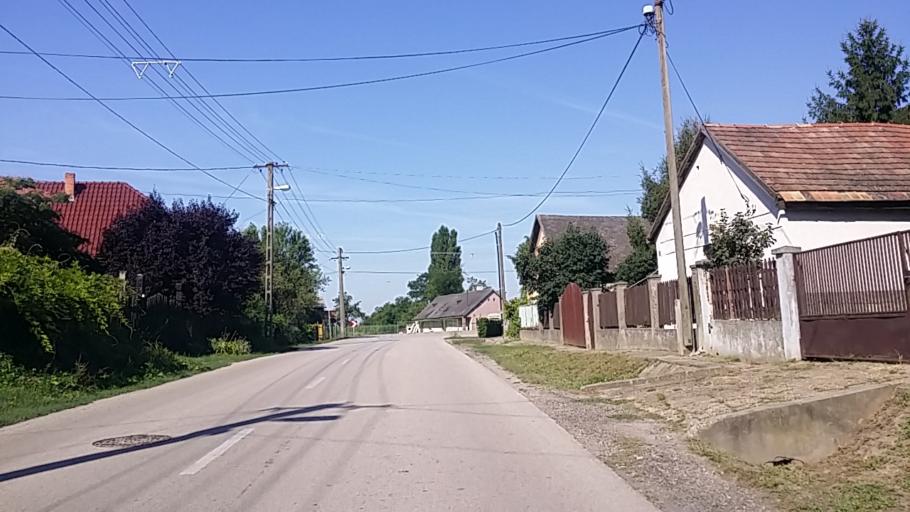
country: HU
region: Fejer
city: Ivancsa
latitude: 47.1395
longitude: 18.8376
